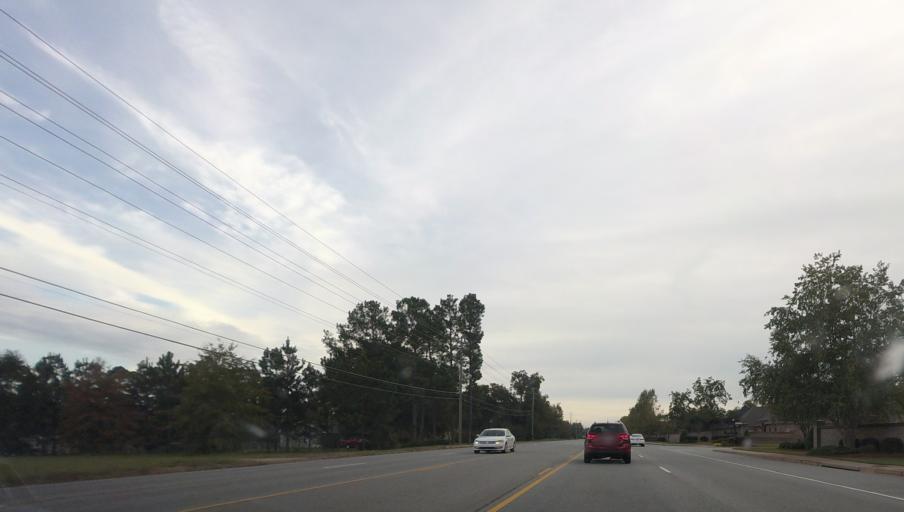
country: US
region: Georgia
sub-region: Houston County
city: Centerville
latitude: 32.5695
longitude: -83.6912
